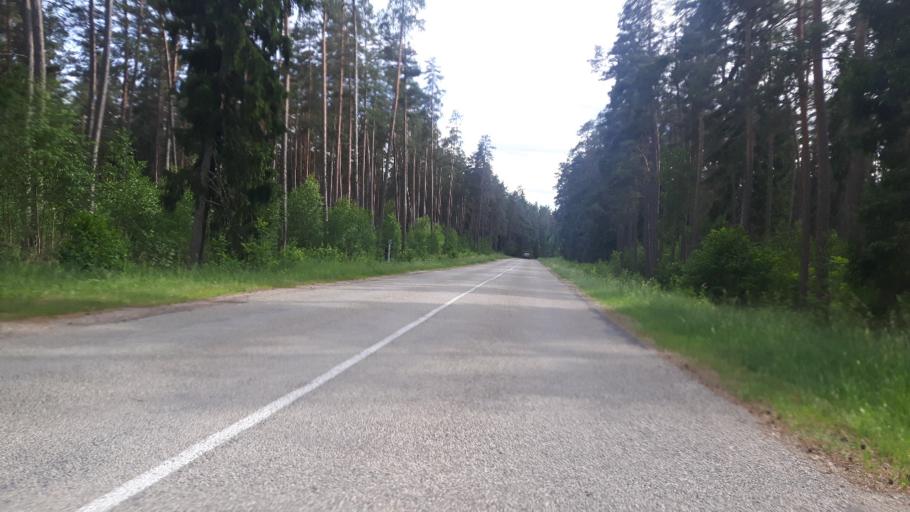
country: LV
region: Engure
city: Smarde
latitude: 57.0043
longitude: 23.3329
